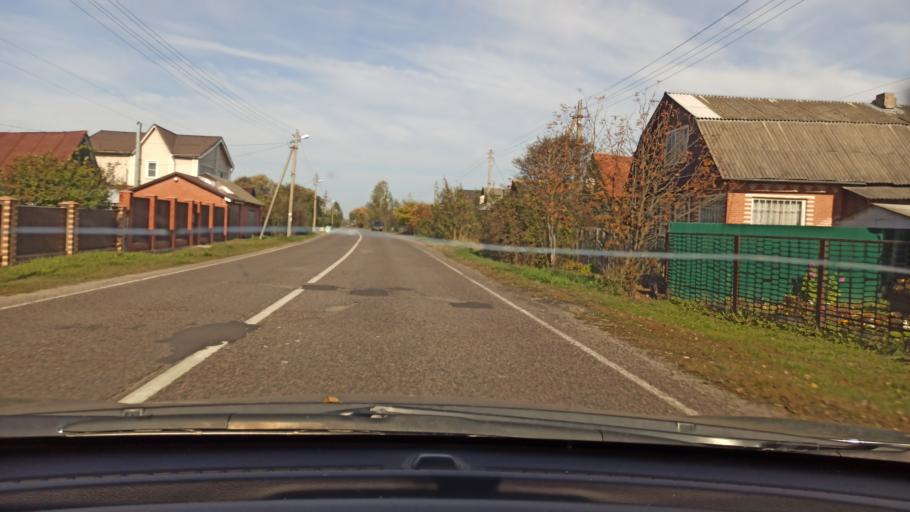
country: RU
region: Moskovskaya
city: Novoye
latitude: 55.6236
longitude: 38.9639
